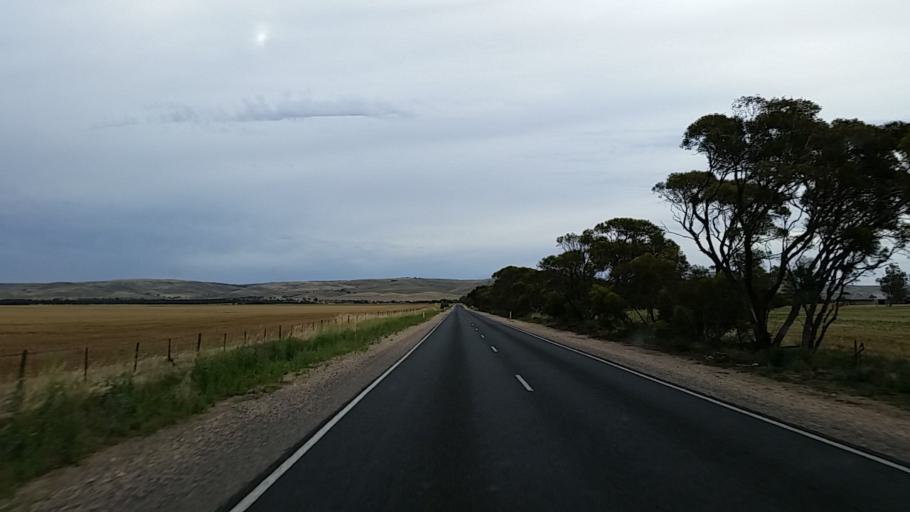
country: AU
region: South Australia
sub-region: Mid Murray
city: Mannum
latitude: -34.7555
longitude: 139.2414
